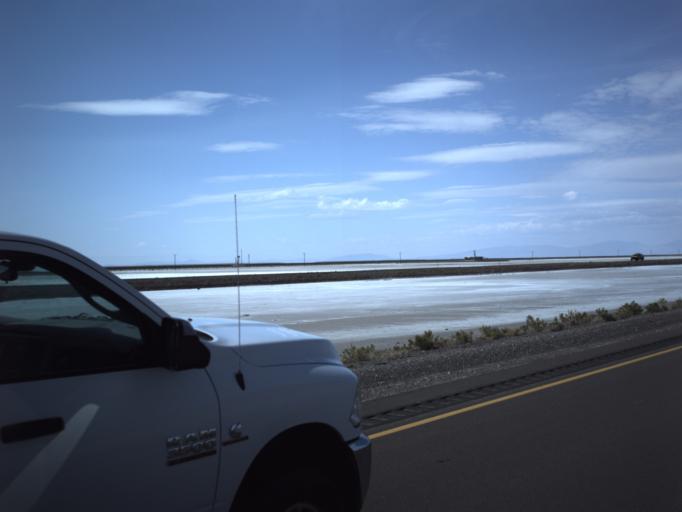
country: US
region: Utah
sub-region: Tooele County
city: Wendover
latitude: 40.7302
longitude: -113.4300
